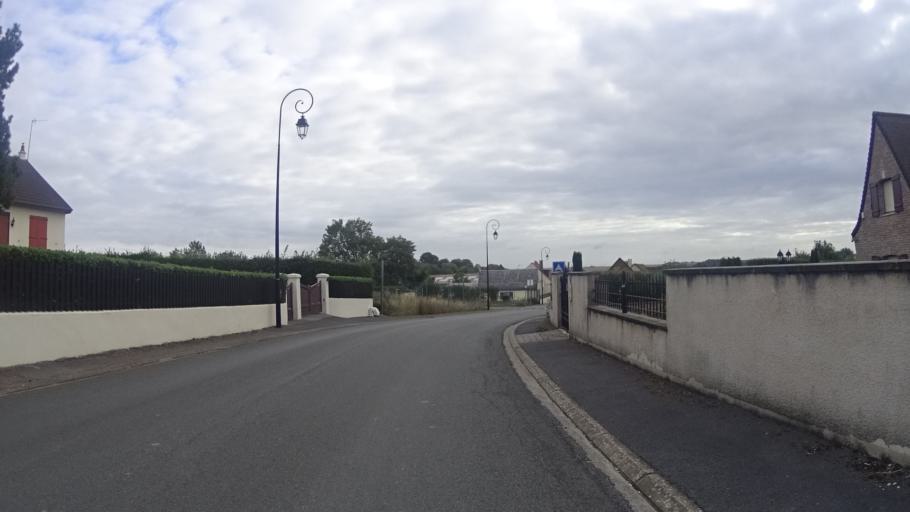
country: FR
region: Picardie
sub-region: Departement de l'Aisne
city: Etreux
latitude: 49.9553
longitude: 3.5995
